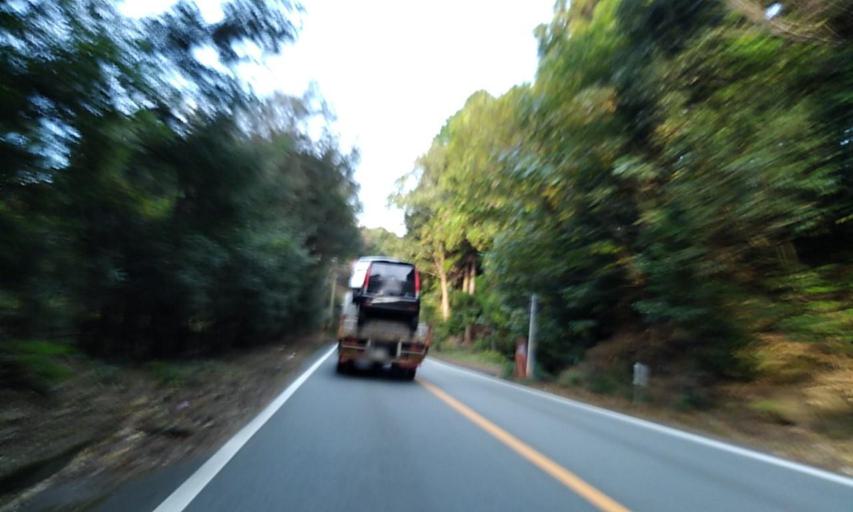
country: JP
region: Mie
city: Toba
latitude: 34.4044
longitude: 136.7789
